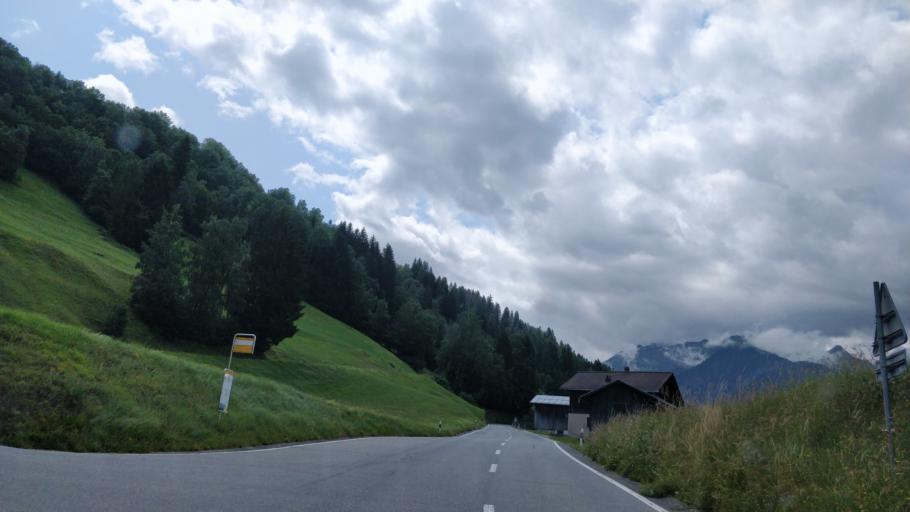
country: CH
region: Grisons
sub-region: Surselva District
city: Ilanz
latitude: 46.7123
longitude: 9.1951
